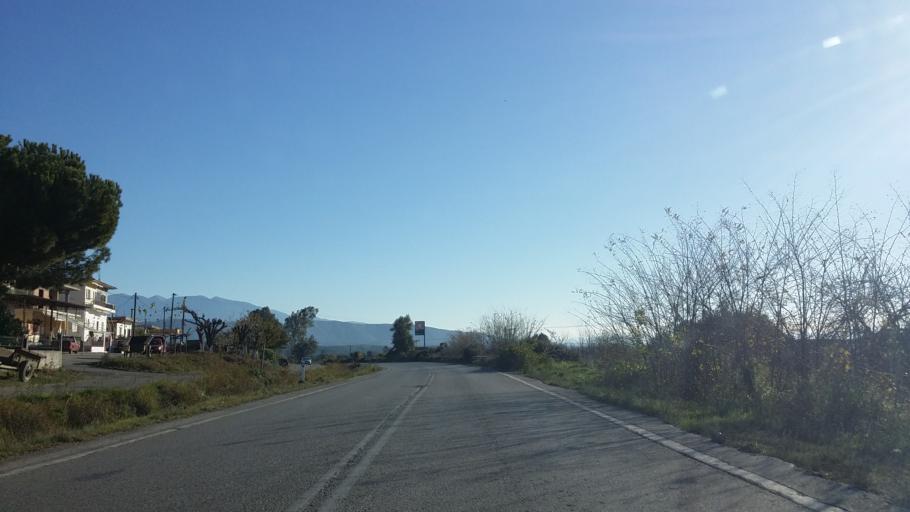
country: GR
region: West Greece
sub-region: Nomos Aitolias kai Akarnanias
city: Lepenou
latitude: 38.6661
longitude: 21.3091
